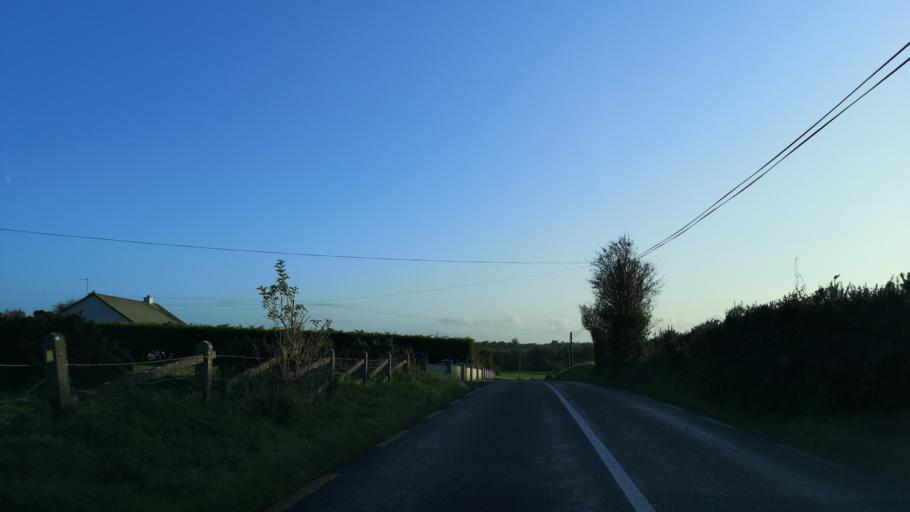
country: IE
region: Connaught
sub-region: Roscommon
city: Castlerea
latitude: 53.7006
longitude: -8.5687
